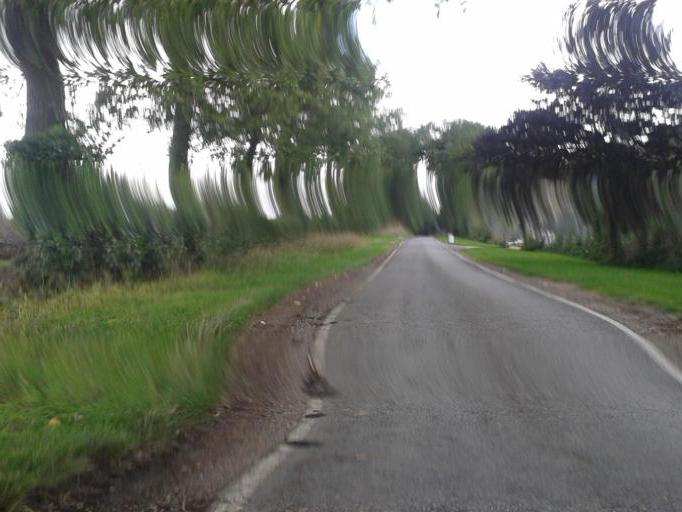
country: GB
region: England
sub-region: Cambridgeshire
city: Duxford
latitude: 51.9996
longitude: 0.1105
